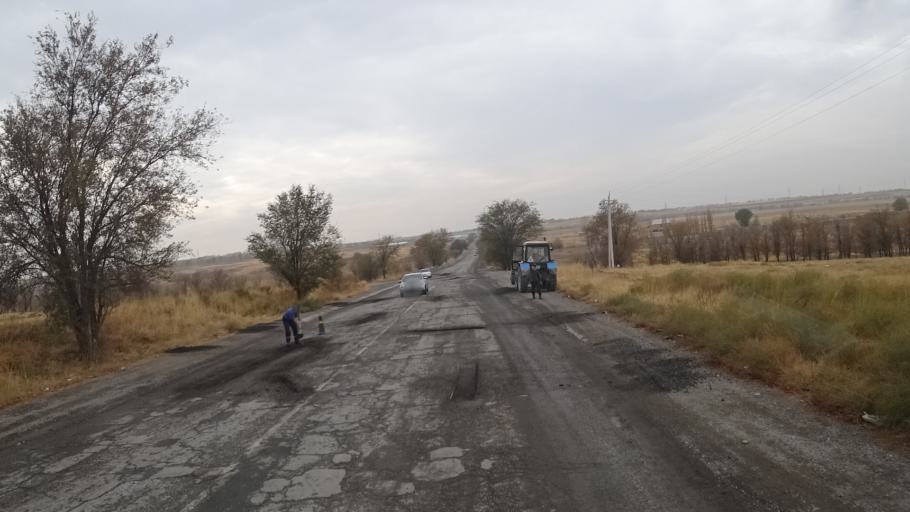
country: KZ
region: Ongtustik Qazaqstan
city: Aksu
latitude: 42.4281
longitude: 69.7072
